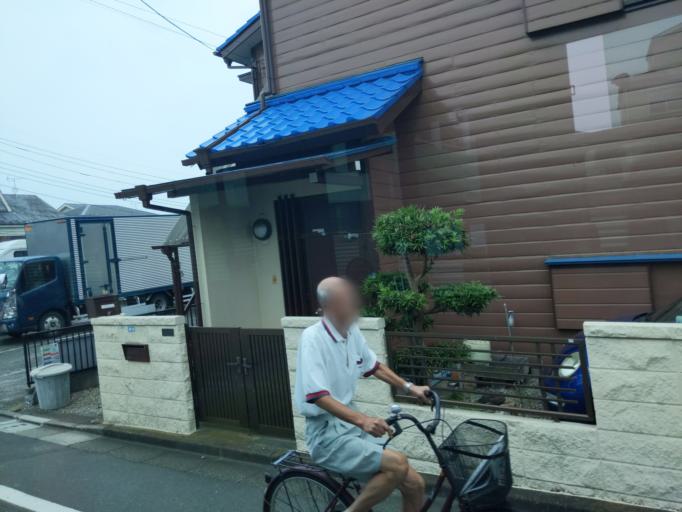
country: JP
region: Saitama
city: Wako
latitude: 35.7724
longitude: 139.6552
